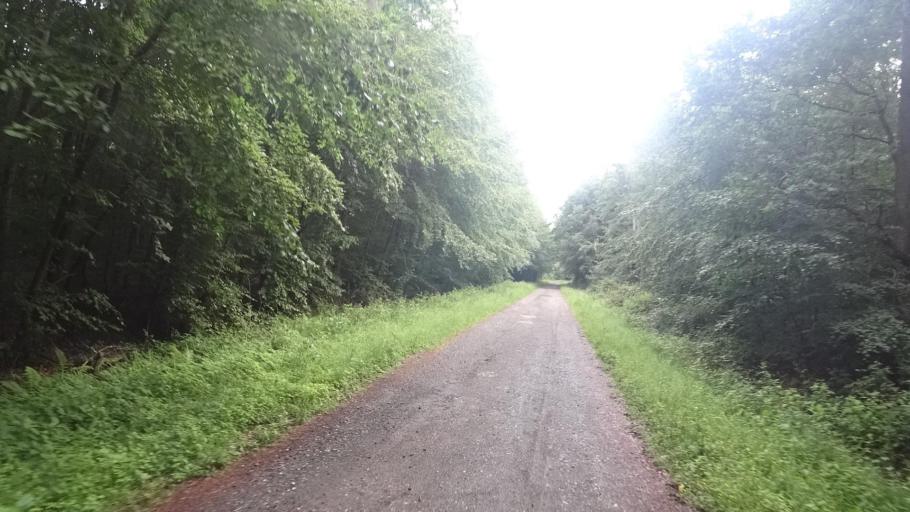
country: DE
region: Rheinland-Pfalz
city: Dernau
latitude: 50.5575
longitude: 7.0671
